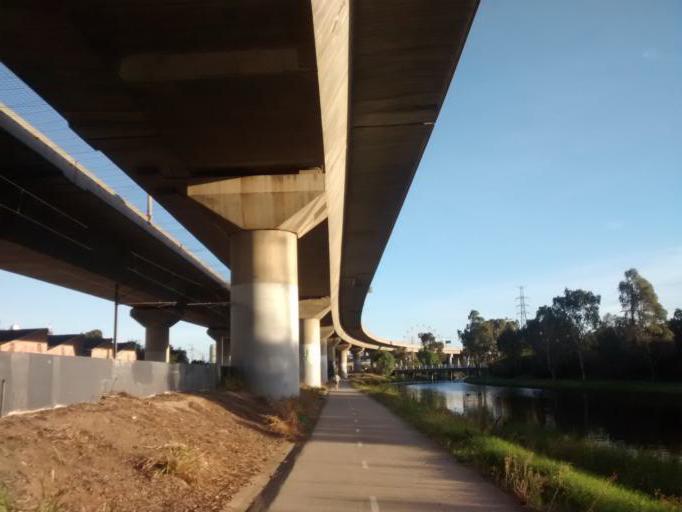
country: AU
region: Victoria
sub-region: Moonee Valley
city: Flemington
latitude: -37.7971
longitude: 144.9360
